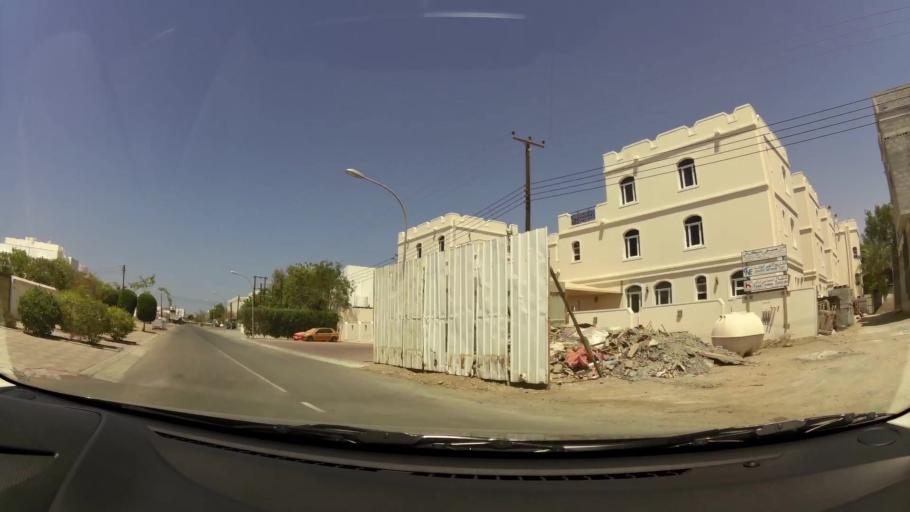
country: OM
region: Muhafazat Masqat
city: As Sib al Jadidah
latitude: 23.6306
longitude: 58.2288
